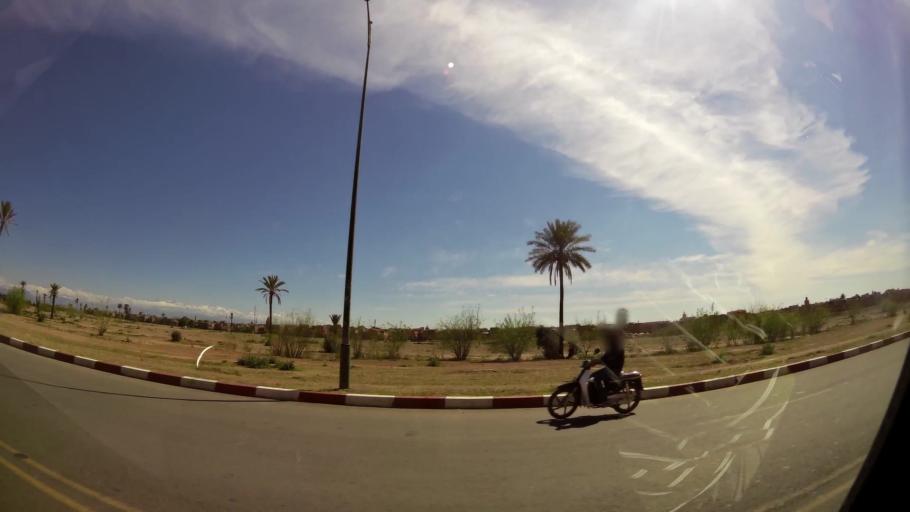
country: MA
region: Marrakech-Tensift-Al Haouz
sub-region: Marrakech
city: Marrakesh
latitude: 31.6201
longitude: -7.9629
